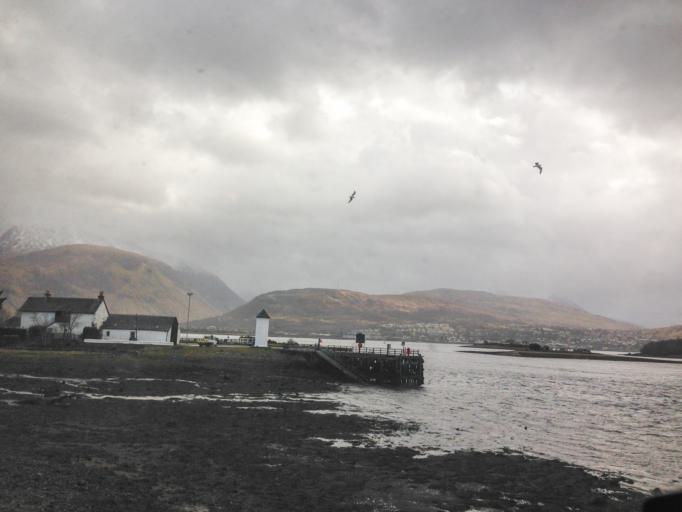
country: GB
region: Scotland
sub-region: Highland
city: Fort William
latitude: 56.8428
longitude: -5.1254
